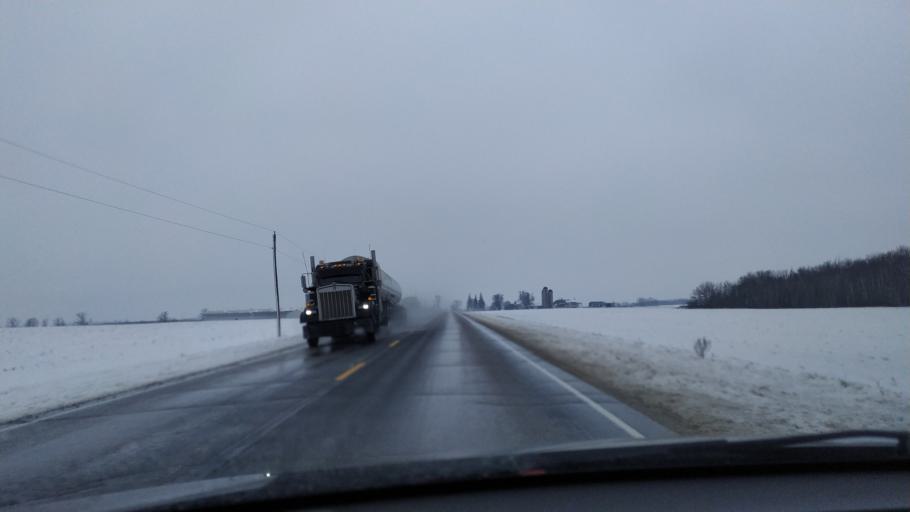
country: CA
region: Ontario
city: North Perth
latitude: 43.5948
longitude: -80.8218
